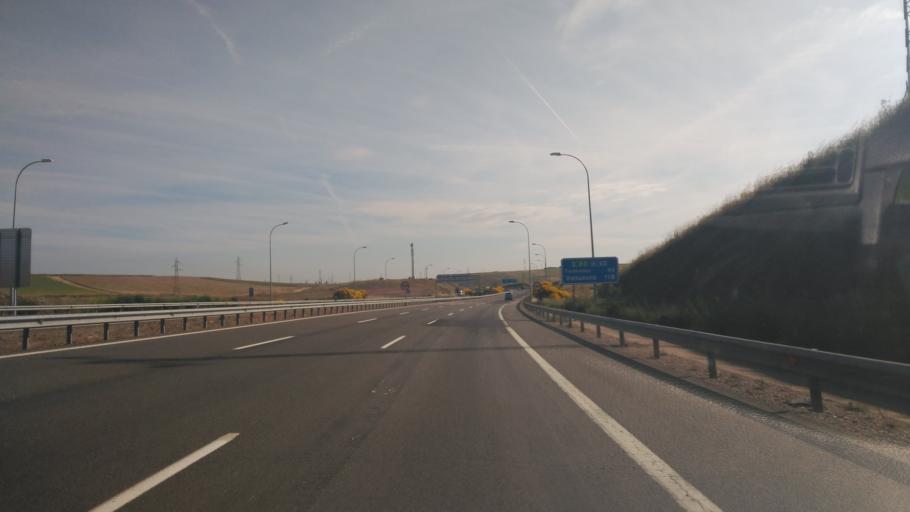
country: ES
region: Castille and Leon
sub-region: Provincia de Salamanca
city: Villamayor
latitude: 40.9683
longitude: -5.6982
